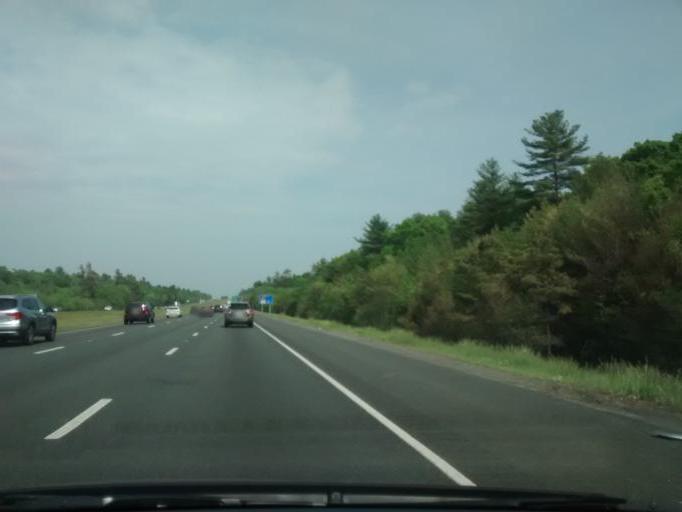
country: US
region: Massachusetts
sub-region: Bristol County
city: Raynham
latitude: 41.9606
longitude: -71.0977
